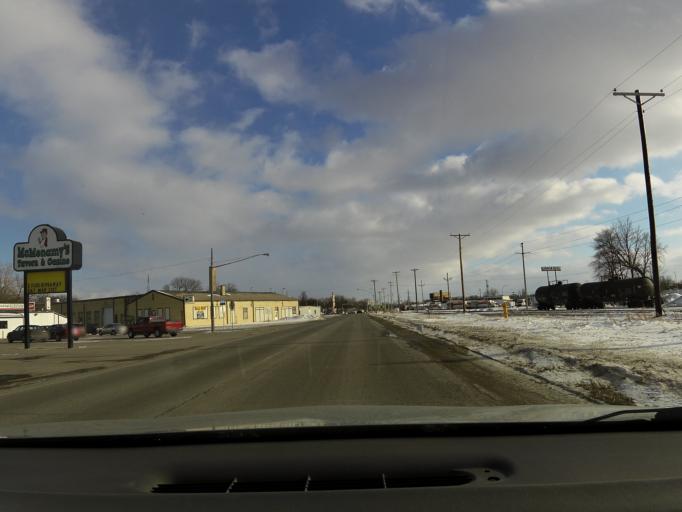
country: US
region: North Dakota
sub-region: Grand Forks County
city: Grand Forks
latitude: 47.9355
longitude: -97.0513
